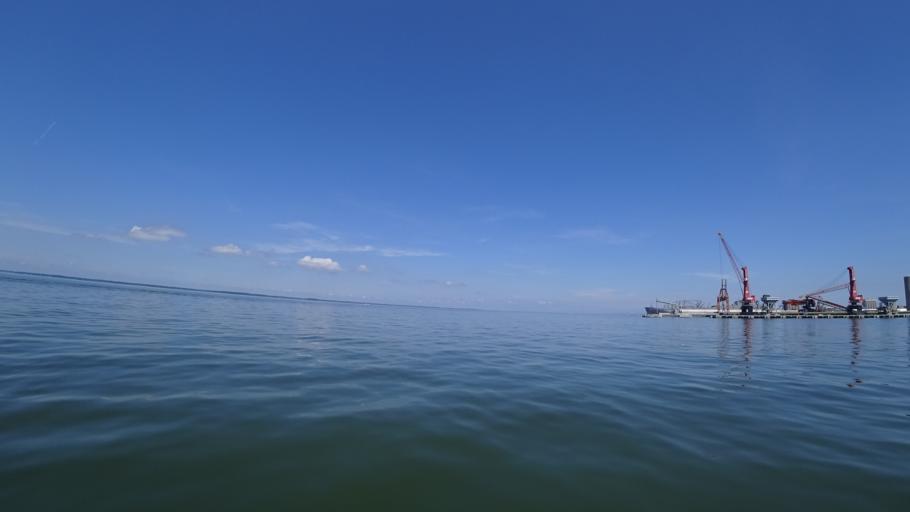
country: US
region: Virginia
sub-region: City of Newport News
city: Newport News
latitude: 36.9626
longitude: -76.4266
